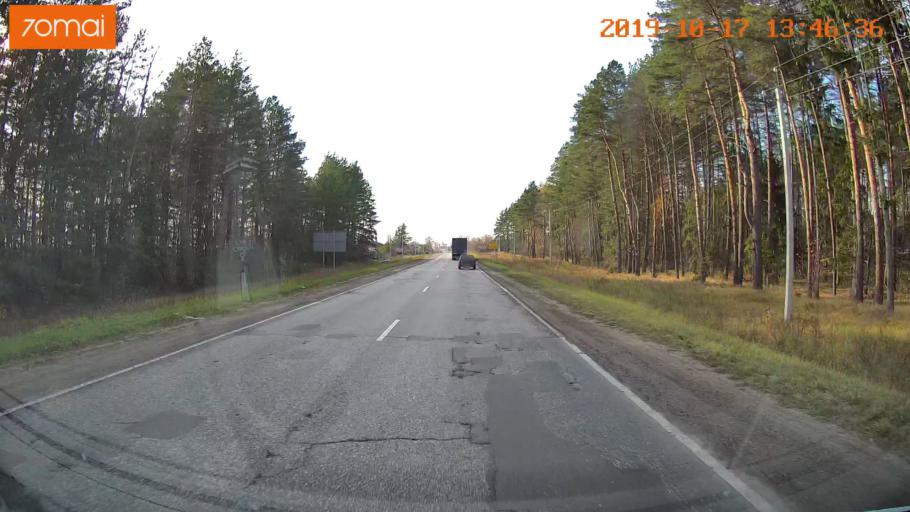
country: RU
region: Rjazan
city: Tuma
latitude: 55.1475
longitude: 40.4856
